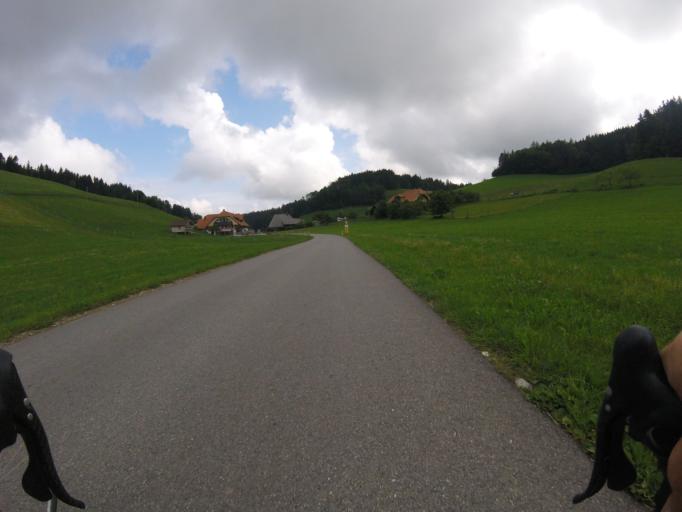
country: CH
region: Bern
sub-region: Emmental District
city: Krauchthal
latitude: 46.9781
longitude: 7.5802
